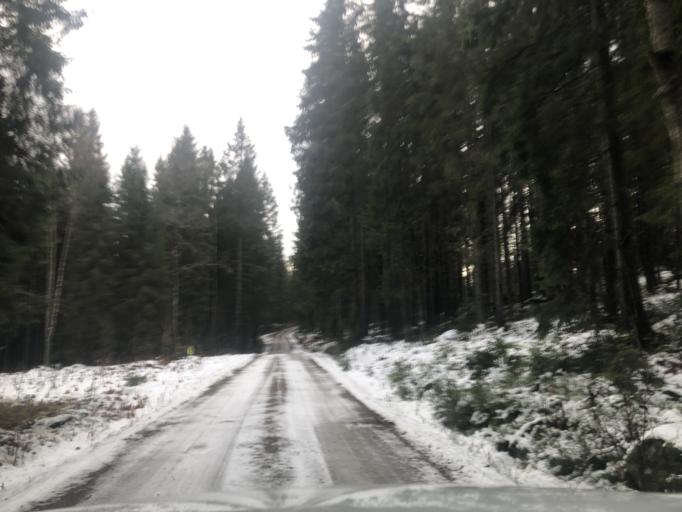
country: SE
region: Vaestra Goetaland
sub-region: Ulricehamns Kommun
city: Ulricehamn
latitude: 57.7839
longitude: 13.4807
